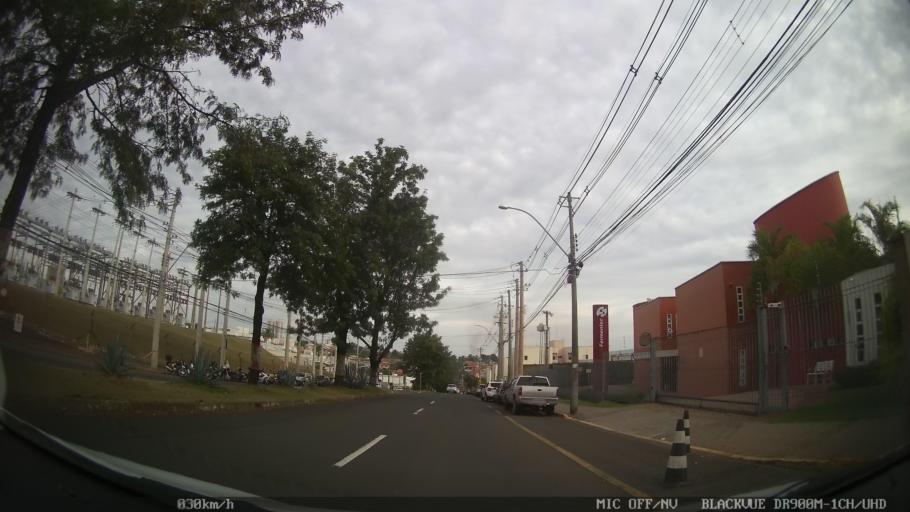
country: BR
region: Sao Paulo
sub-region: Piracicaba
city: Piracicaba
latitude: -22.7303
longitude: -47.6212
